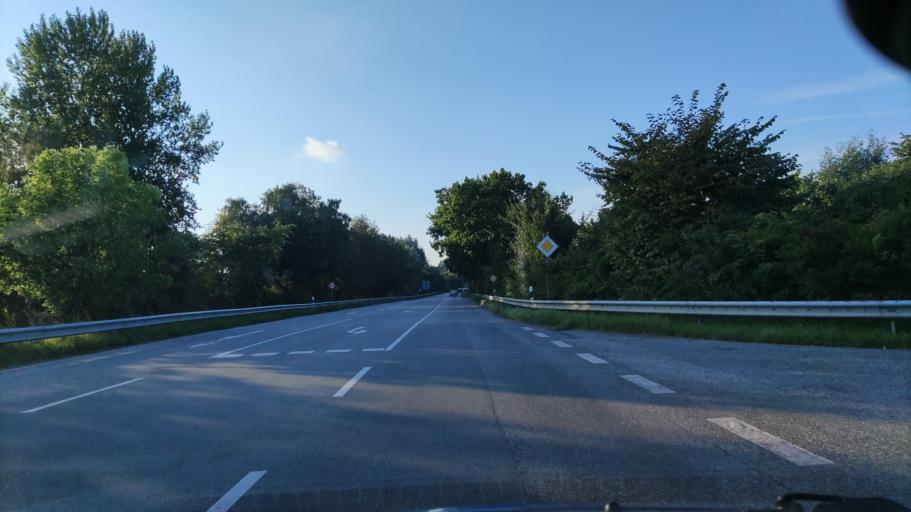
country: DE
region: Schleswig-Holstein
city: Ploen
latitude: 54.1626
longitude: 10.4025
